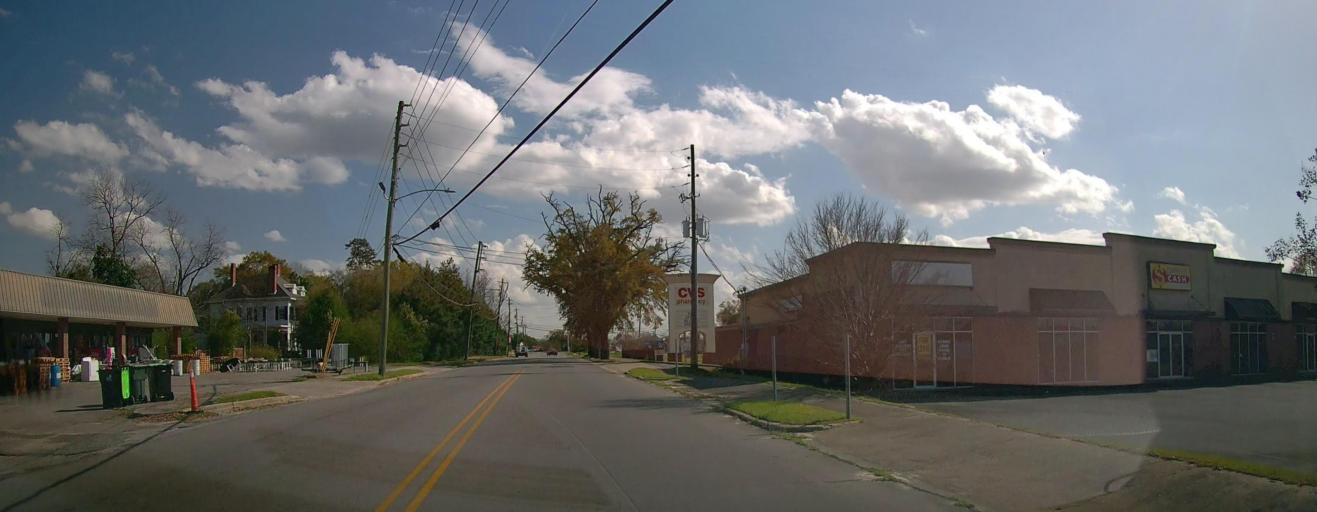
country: US
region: Georgia
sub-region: Dodge County
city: Eastman
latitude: 32.1943
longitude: -83.1750
